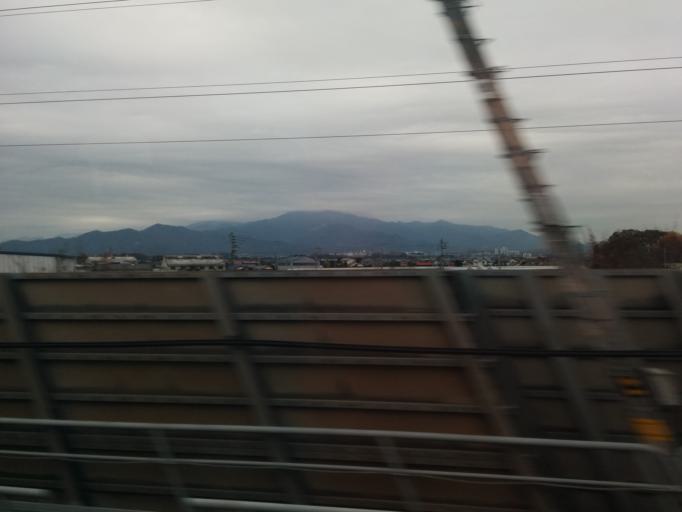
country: JP
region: Kanagawa
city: Isehara
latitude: 35.3739
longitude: 139.3457
